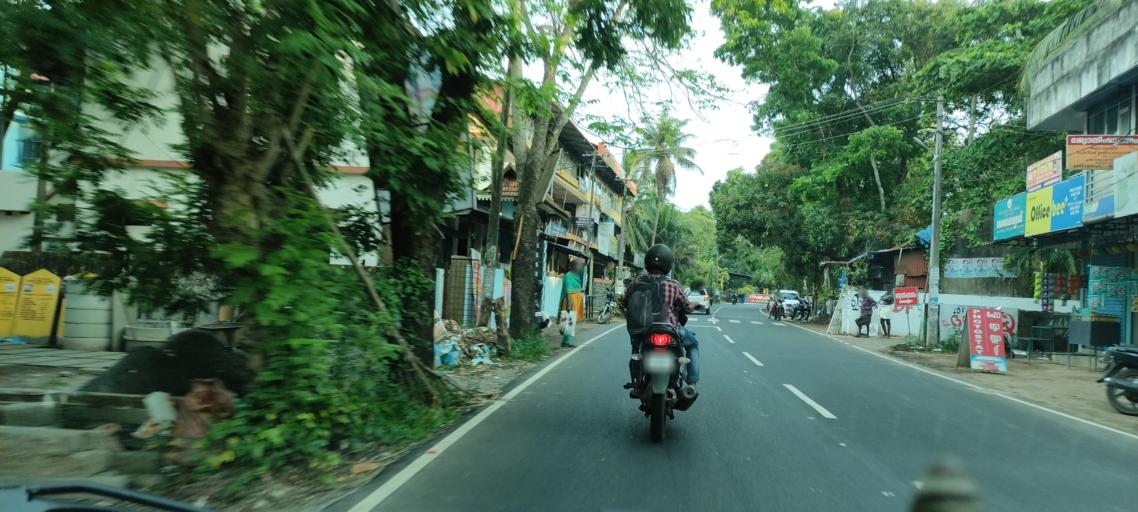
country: IN
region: Kerala
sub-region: Alappuzha
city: Arukutti
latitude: 9.8650
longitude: 76.3240
